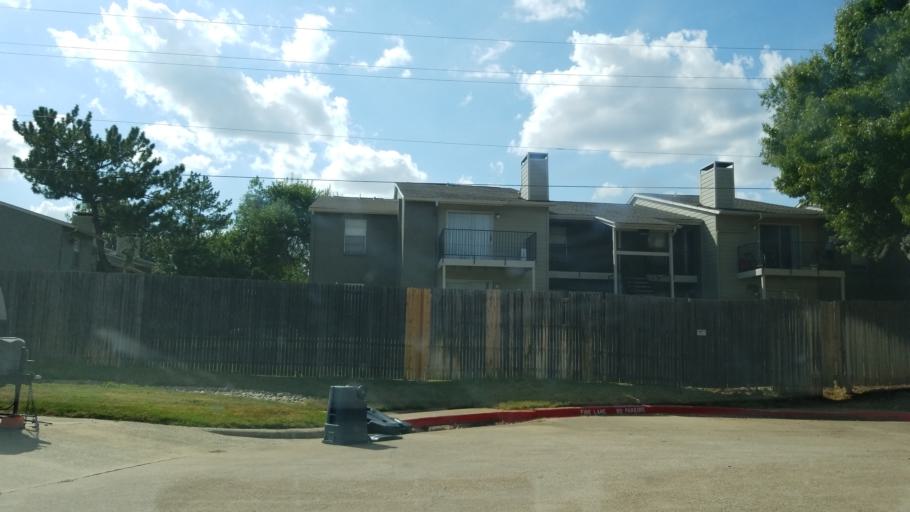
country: US
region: Texas
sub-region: Tarrant County
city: Euless
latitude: 32.8558
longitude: -97.0780
